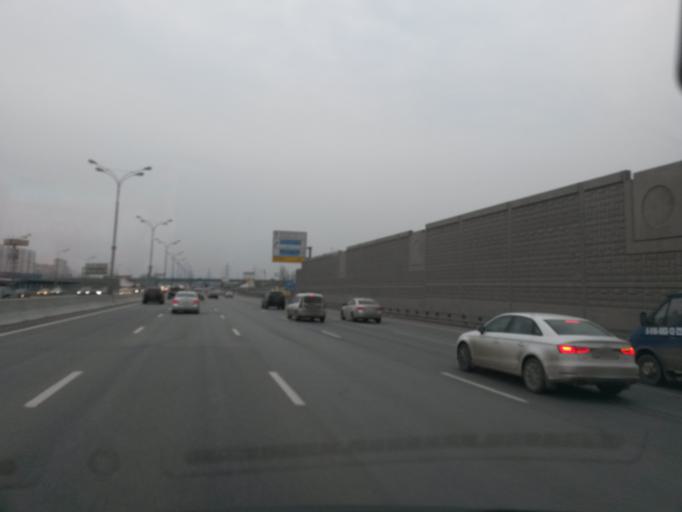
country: RU
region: Moscow
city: Vostochnyy
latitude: 55.8091
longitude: 37.8395
